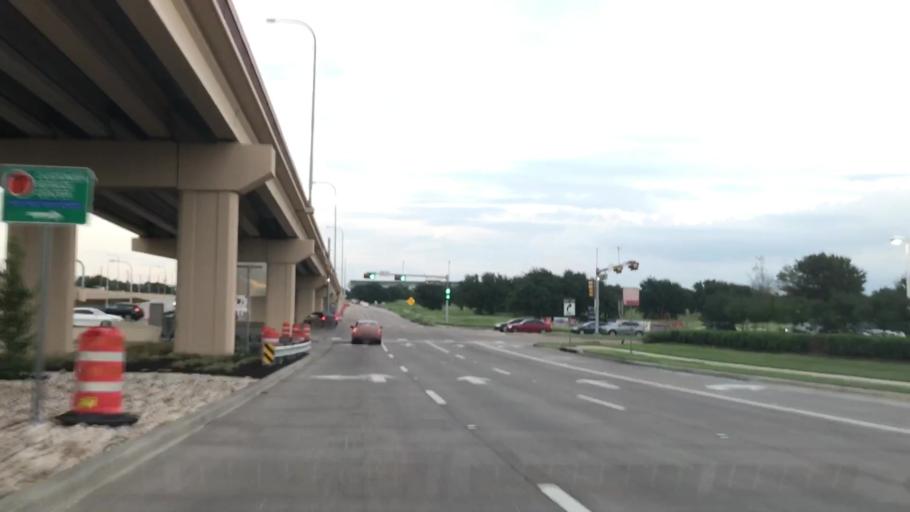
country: US
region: Texas
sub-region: Dallas County
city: Addison
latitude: 33.0156
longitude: -96.8286
